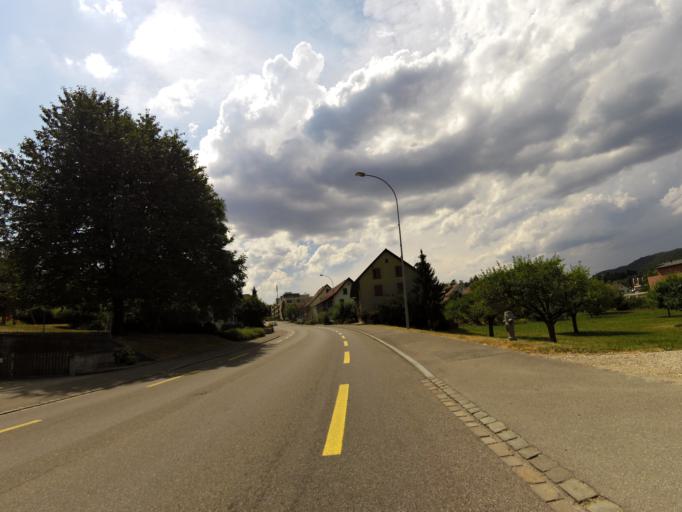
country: CH
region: Aargau
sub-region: Bezirk Lenzburg
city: Othmarsingen
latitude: 47.4106
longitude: 8.2266
